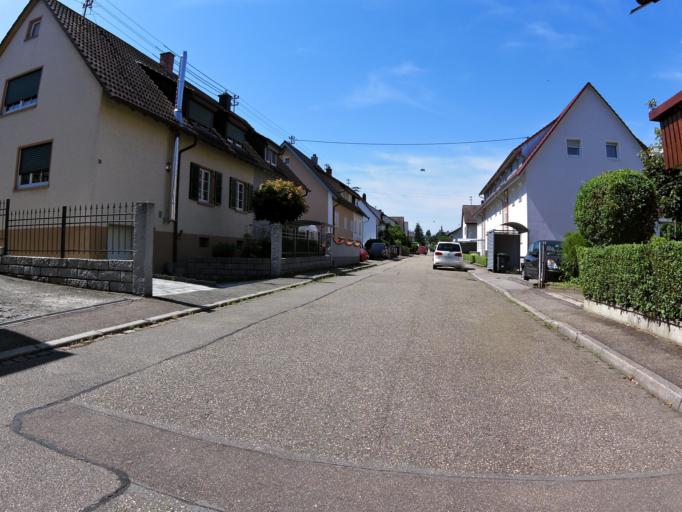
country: DE
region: Baden-Wuerttemberg
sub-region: Freiburg Region
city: Lahr
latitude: 48.3309
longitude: 7.8459
